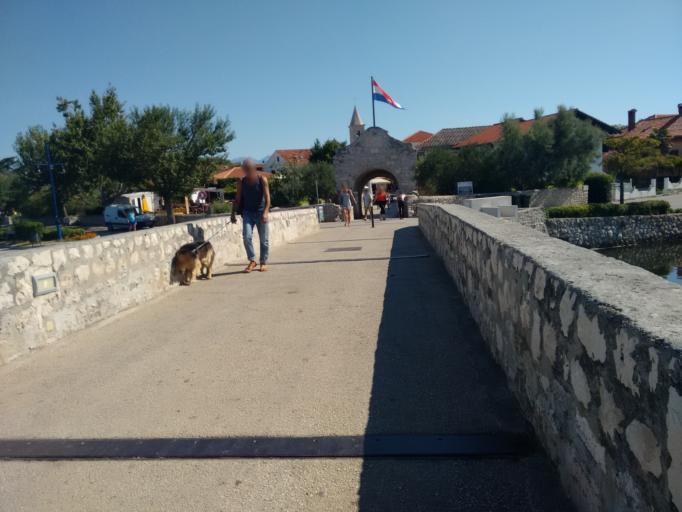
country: HR
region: Zadarska
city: Nin
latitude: 44.2414
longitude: 15.1816
